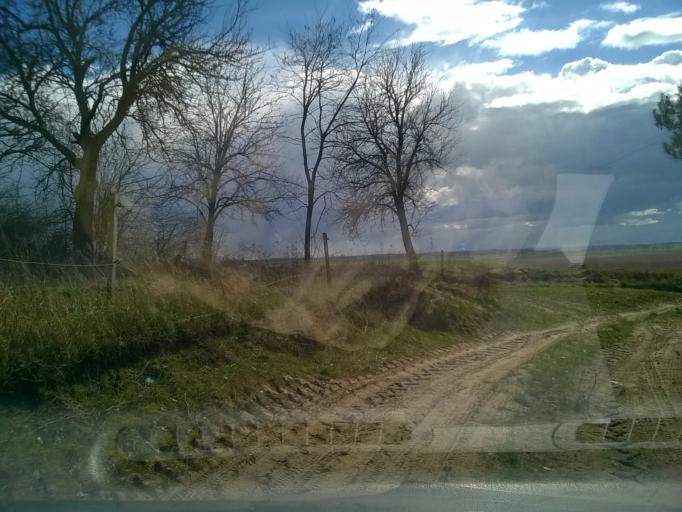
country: PL
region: Kujawsko-Pomorskie
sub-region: Powiat nakielski
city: Kcynia
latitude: 53.0276
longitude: 17.4074
